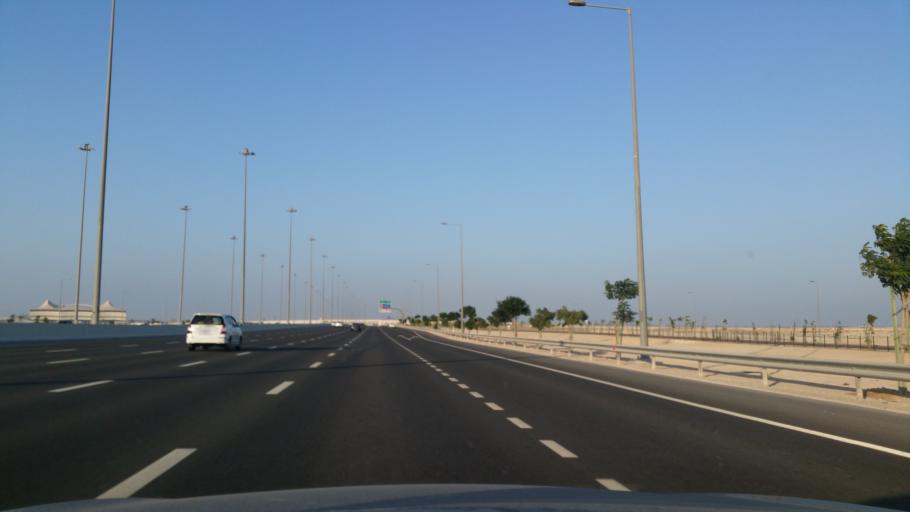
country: QA
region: Baladiyat az Za`ayin
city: Az Za`ayin
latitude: 25.6272
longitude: 51.4874
